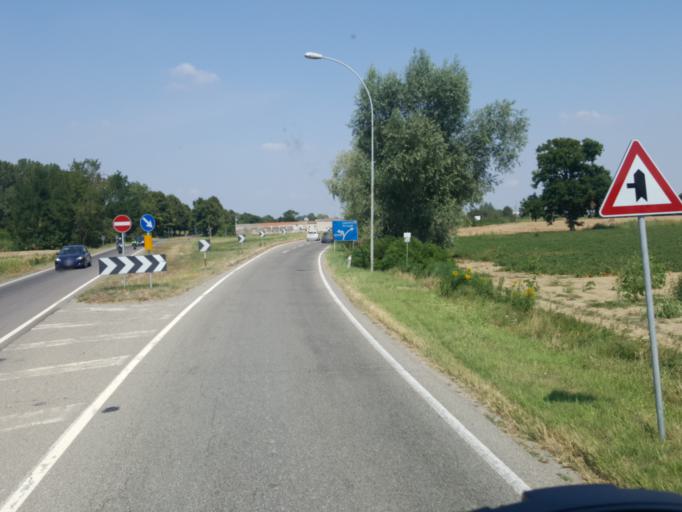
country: IT
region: Emilia-Romagna
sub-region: Provincia di Piacenza
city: Caorso
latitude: 45.0663
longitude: 9.8873
